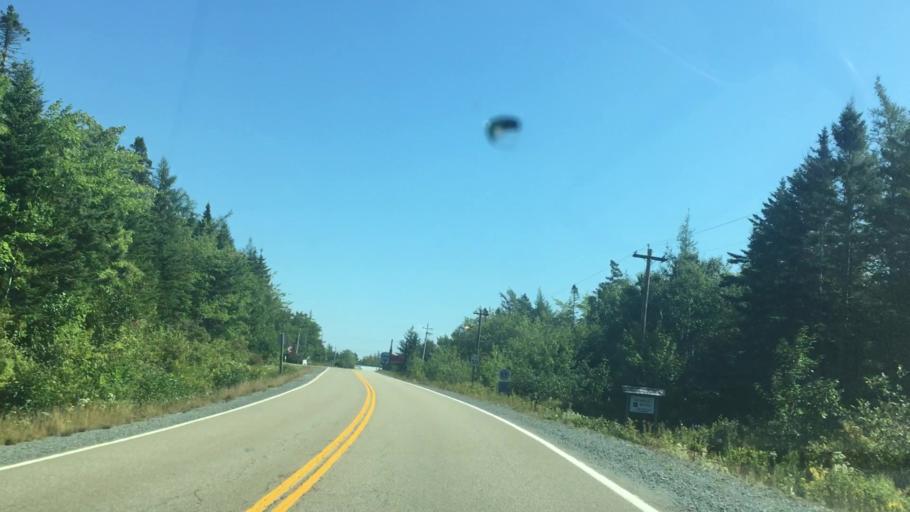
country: CA
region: Nova Scotia
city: Antigonish
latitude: 45.1443
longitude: -61.9932
